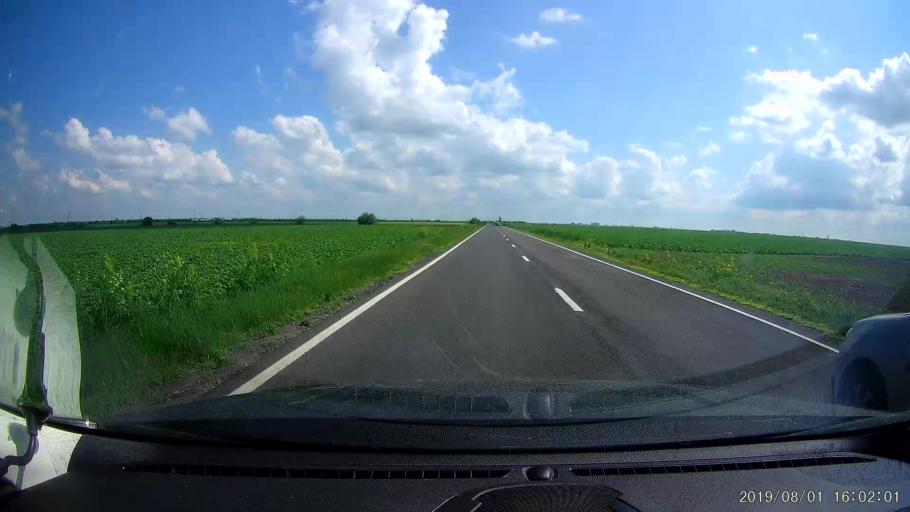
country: RO
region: Ialomita
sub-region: Comuna Ciulnita
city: Ciulnita
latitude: 44.4981
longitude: 27.3888
